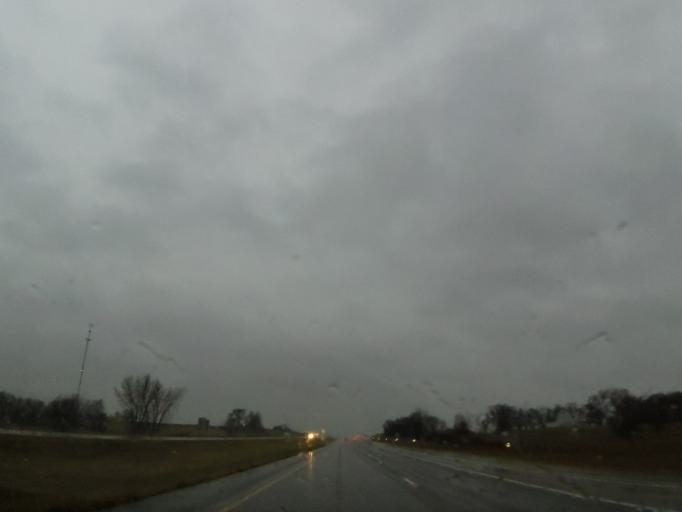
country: US
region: Iowa
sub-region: Worth County
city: Manly
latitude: 43.2882
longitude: -93.3498
